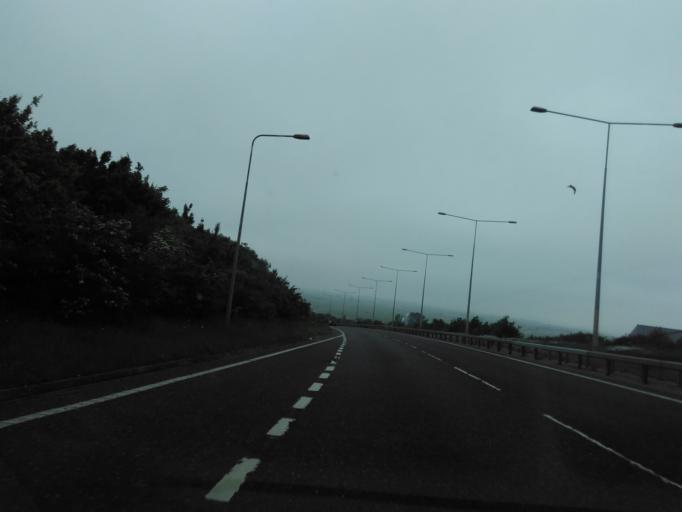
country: GB
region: England
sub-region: Kent
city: Whitstable
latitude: 51.3403
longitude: 1.0133
